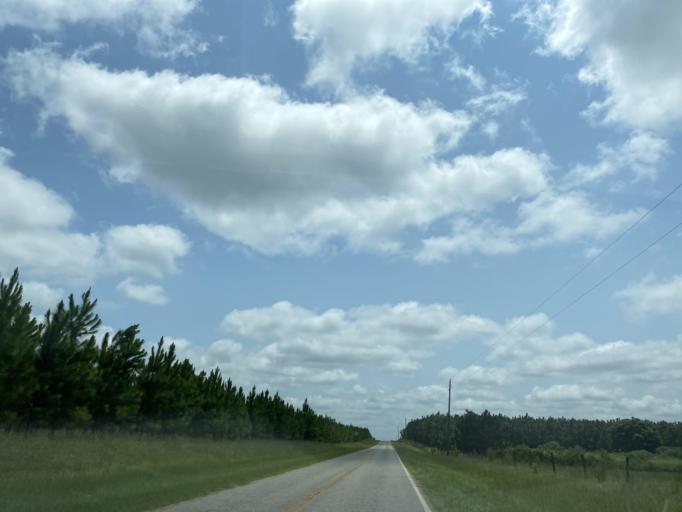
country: US
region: Georgia
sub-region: Wheeler County
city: Alamo
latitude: 32.0679
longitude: -82.7296
